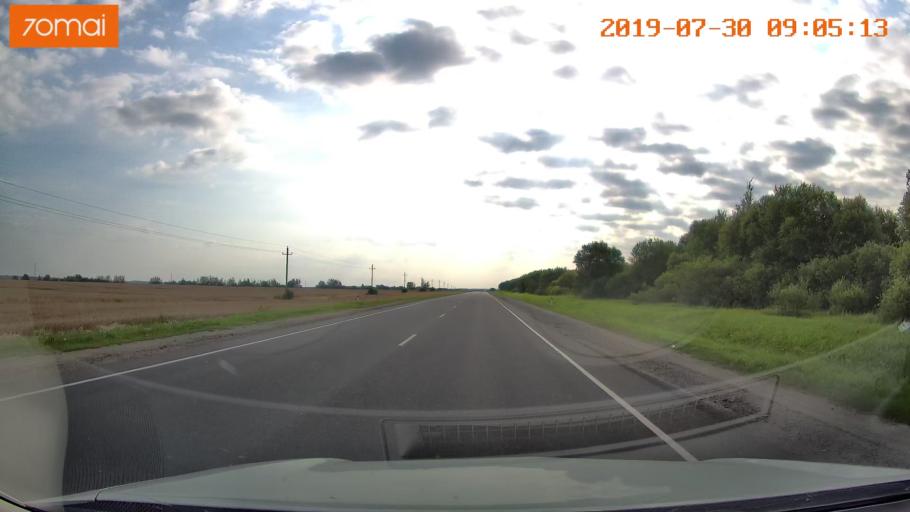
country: RU
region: Kaliningrad
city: Gusev
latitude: 54.6068
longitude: 22.3024
